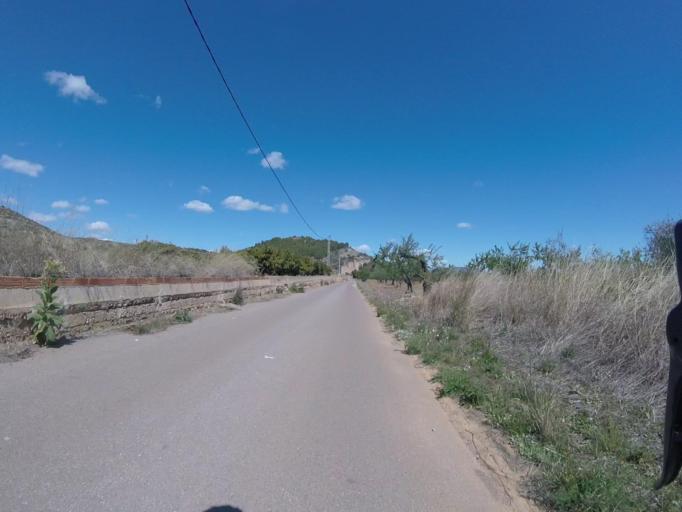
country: ES
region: Valencia
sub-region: Provincia de Castello
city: Torreblanca
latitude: 40.1673
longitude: 0.1572
